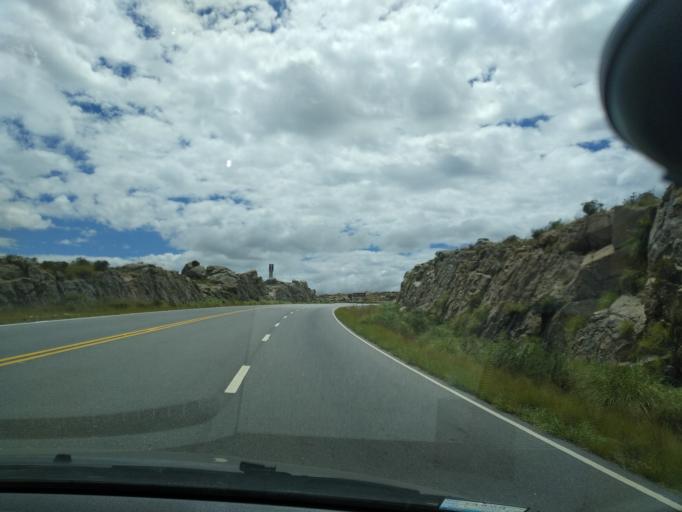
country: AR
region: Cordoba
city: Villa Cura Brochero
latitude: -31.6137
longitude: -64.9087
